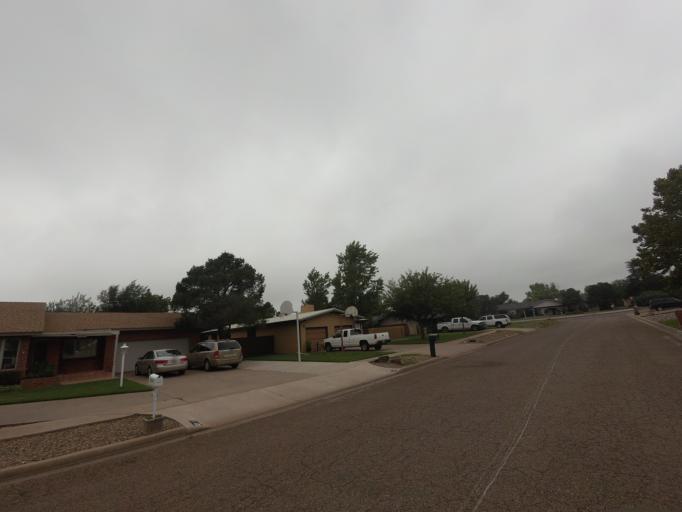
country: US
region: New Mexico
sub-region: Curry County
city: Clovis
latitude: 34.4349
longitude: -103.1893
